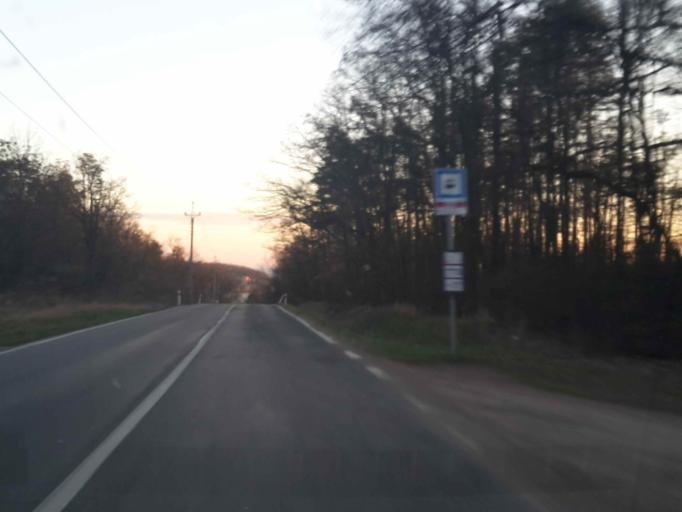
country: CZ
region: South Moravian
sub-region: Mesto Brno
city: Mokra Hora
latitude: 49.2633
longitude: 16.6259
